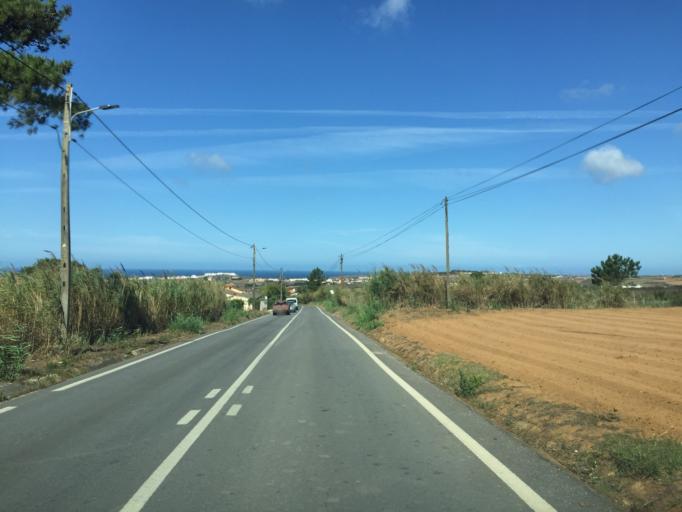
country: PT
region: Lisbon
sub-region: Lourinha
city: Lourinha
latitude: 39.2693
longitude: -9.3006
